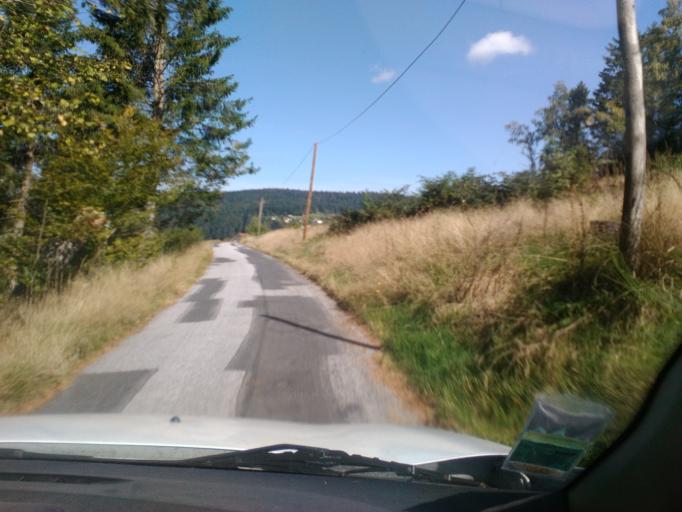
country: FR
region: Lorraine
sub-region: Departement des Vosges
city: Le Tholy
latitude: 48.0727
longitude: 6.7878
